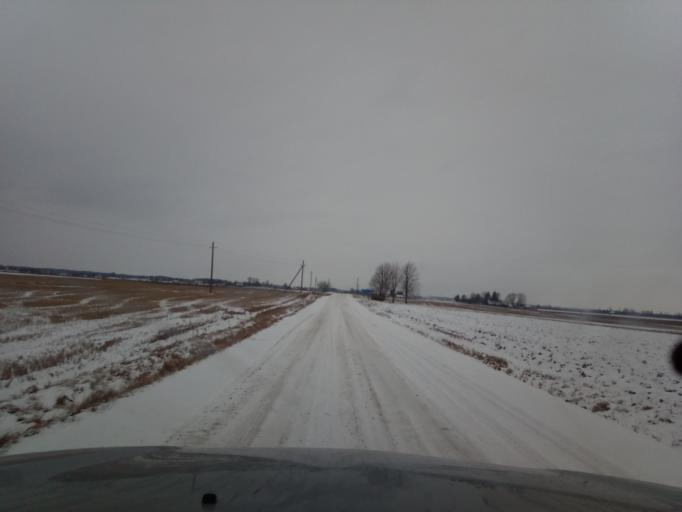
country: LT
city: Ramygala
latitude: 55.4963
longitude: 24.5318
